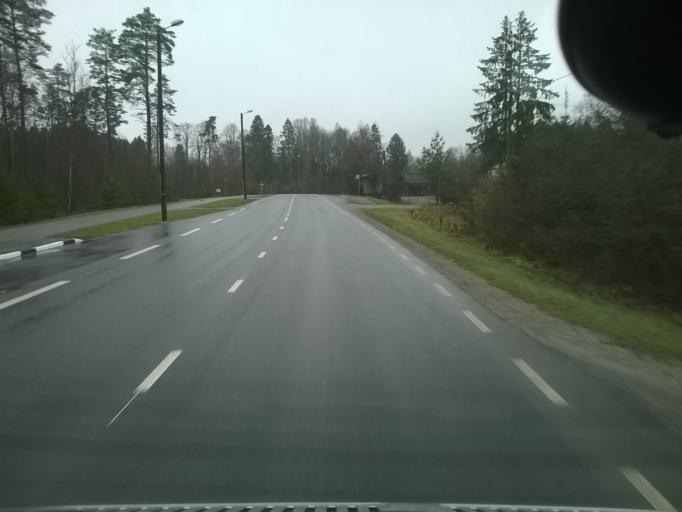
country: EE
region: Harju
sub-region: Saku vald
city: Saku
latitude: 59.2265
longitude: 24.6752
